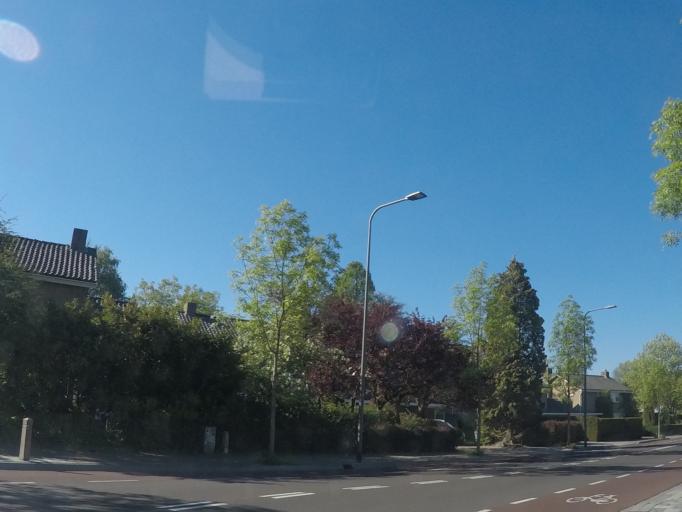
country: NL
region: Gelderland
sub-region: Gemeente Rheden
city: Velp
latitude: 51.9902
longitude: 5.9869
